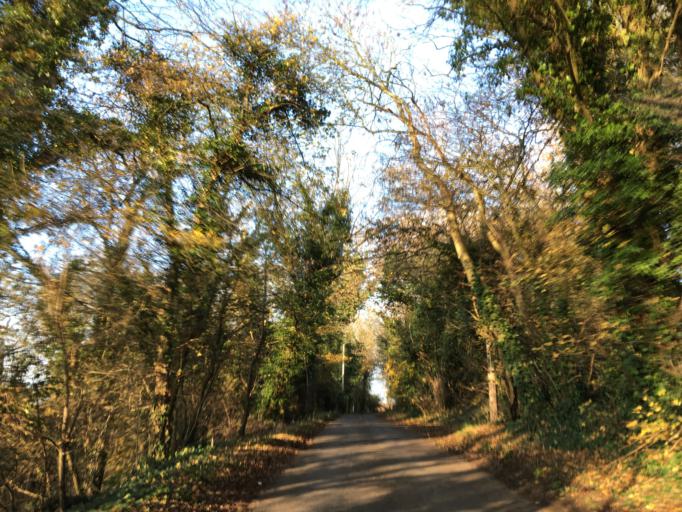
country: GB
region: England
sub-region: South Gloucestershire
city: Yate
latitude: 51.5666
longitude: -2.4068
